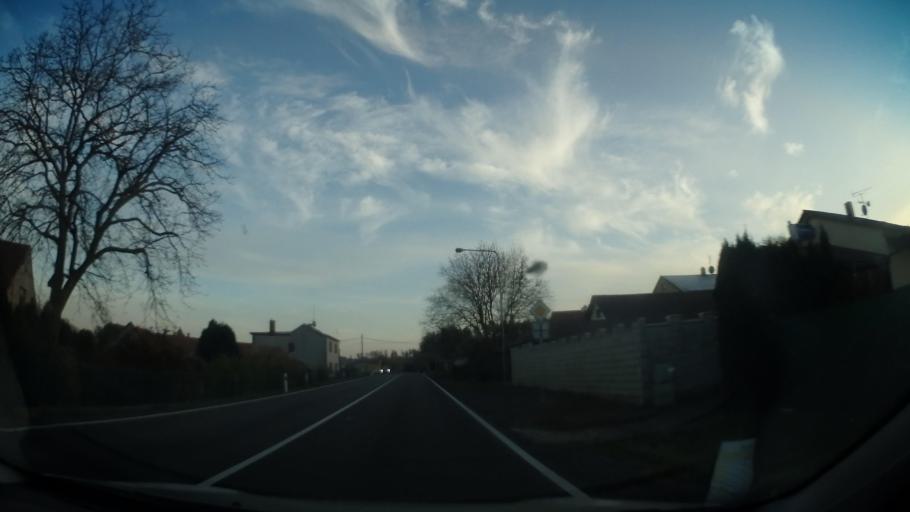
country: CZ
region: Central Bohemia
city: Vlasim
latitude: 49.6813
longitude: 14.9470
